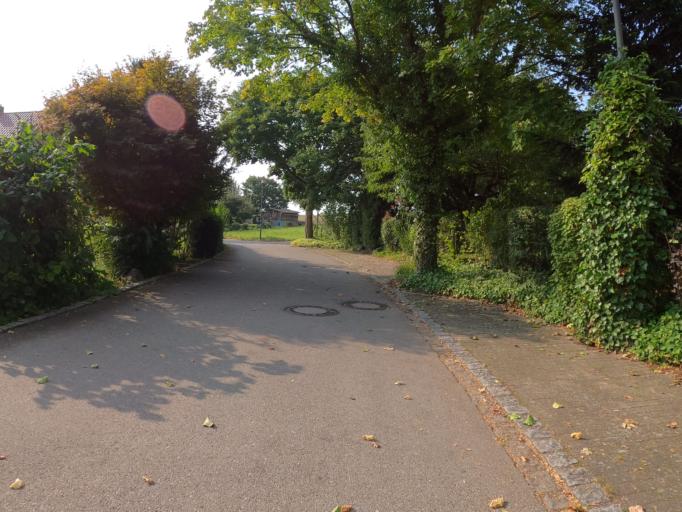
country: DE
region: Bavaria
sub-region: Swabia
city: Offingen
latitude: 48.4854
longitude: 10.3573
